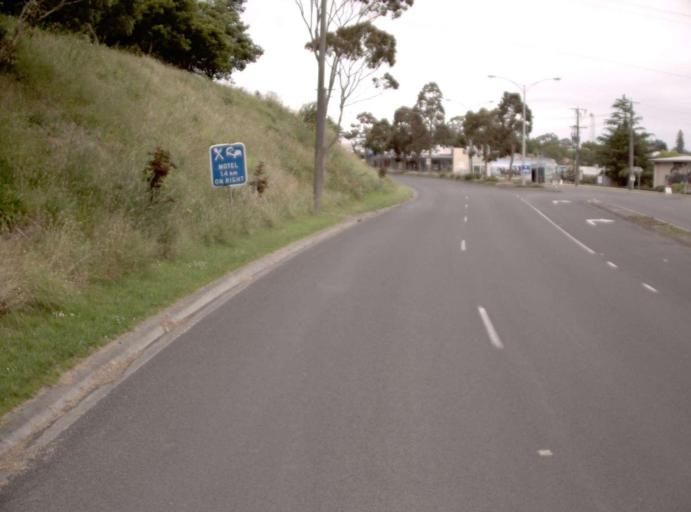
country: AU
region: Victoria
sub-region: Bass Coast
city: North Wonthaggi
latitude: -38.4292
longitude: 145.8215
